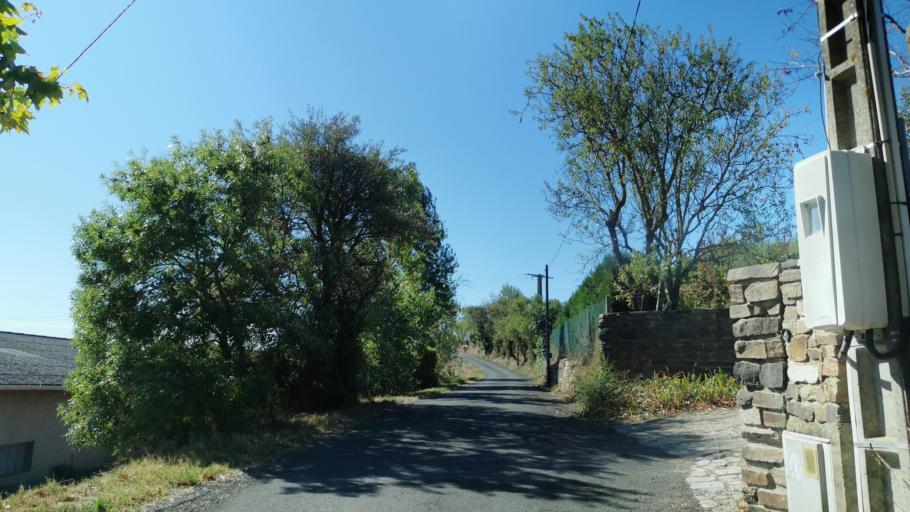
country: FR
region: Languedoc-Roussillon
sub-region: Departement de l'Aude
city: Conques-sur-Orbiel
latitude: 43.2516
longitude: 2.4084
